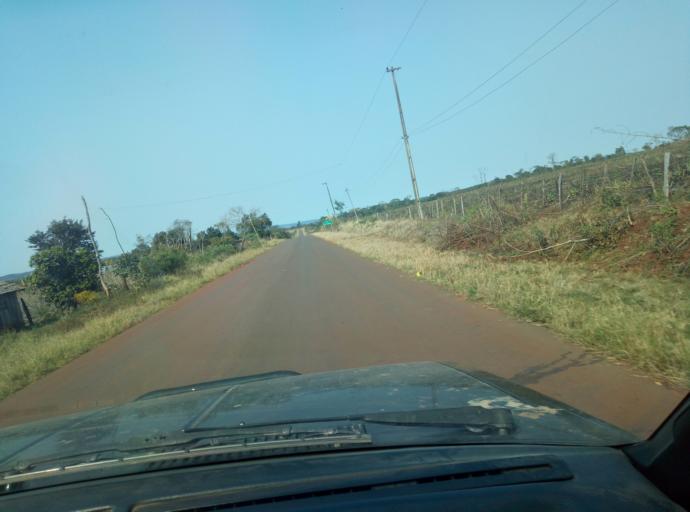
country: PY
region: Caaguazu
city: Carayao
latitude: -25.2207
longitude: -56.2890
